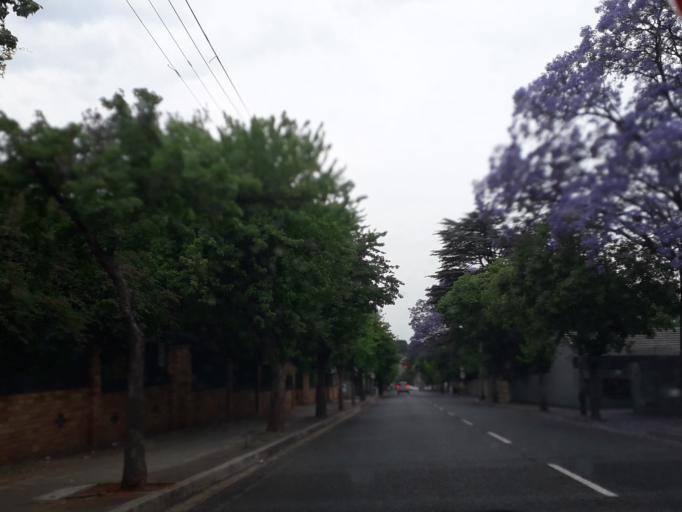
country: ZA
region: Gauteng
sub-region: City of Johannesburg Metropolitan Municipality
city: Johannesburg
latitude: -26.1522
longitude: 28.0770
